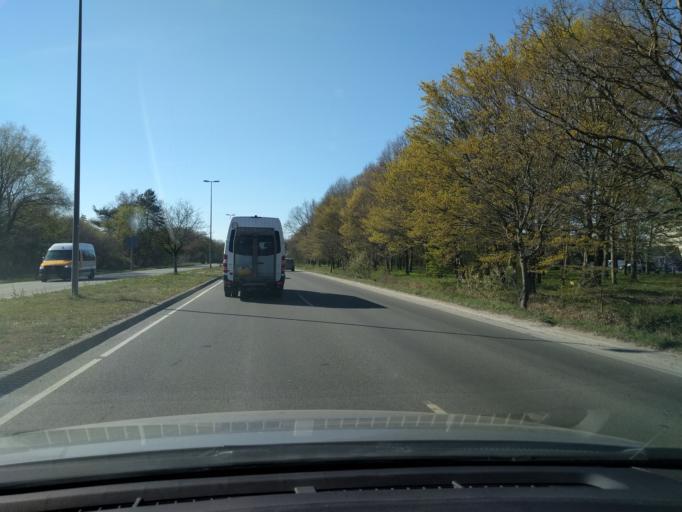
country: DK
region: Zealand
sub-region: Koge Kommune
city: Koge
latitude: 55.4814
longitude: 12.1830
